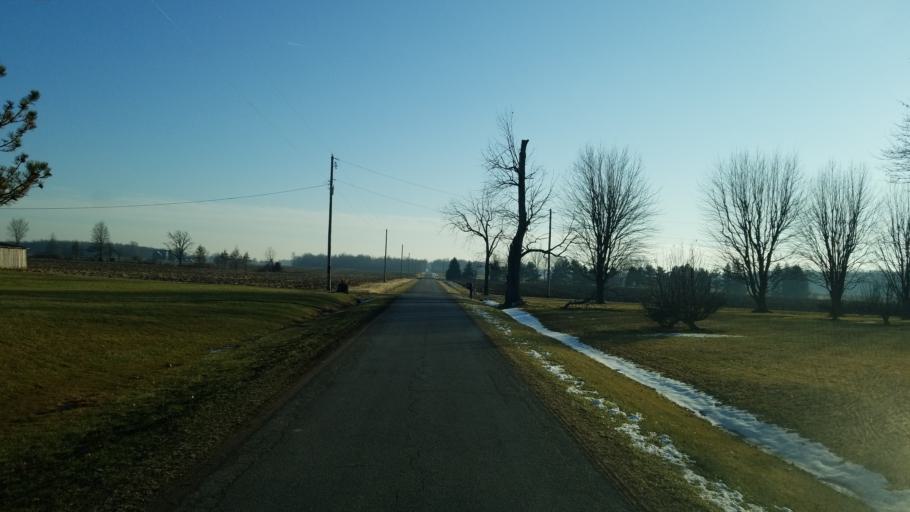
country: US
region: Ohio
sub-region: Crawford County
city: Bucyrus
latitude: 40.9464
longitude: -82.9209
